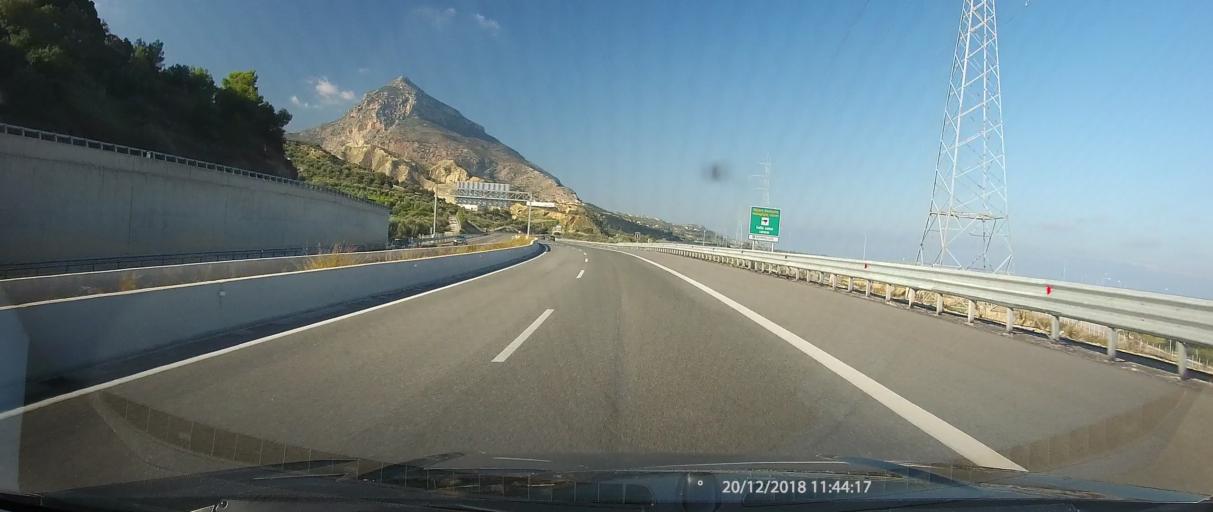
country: GR
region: Peloponnese
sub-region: Nomos Korinthias
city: Xylokastro
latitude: 38.0780
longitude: 22.6046
